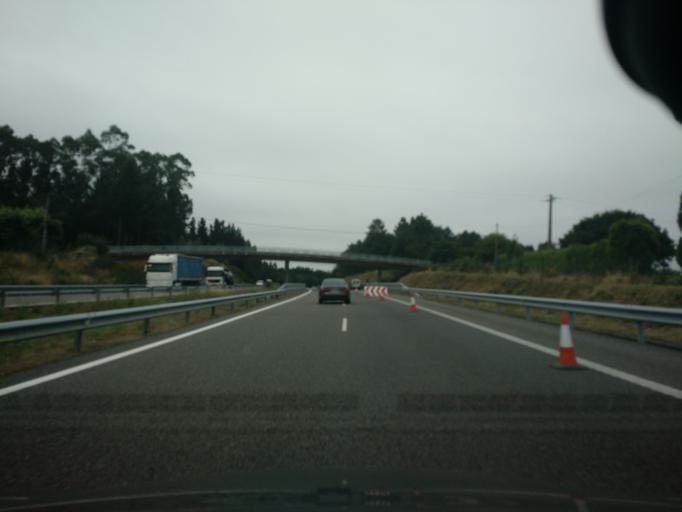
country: ES
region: Galicia
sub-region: Provincia da Coruna
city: Oroso
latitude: 42.9961
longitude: -8.4261
